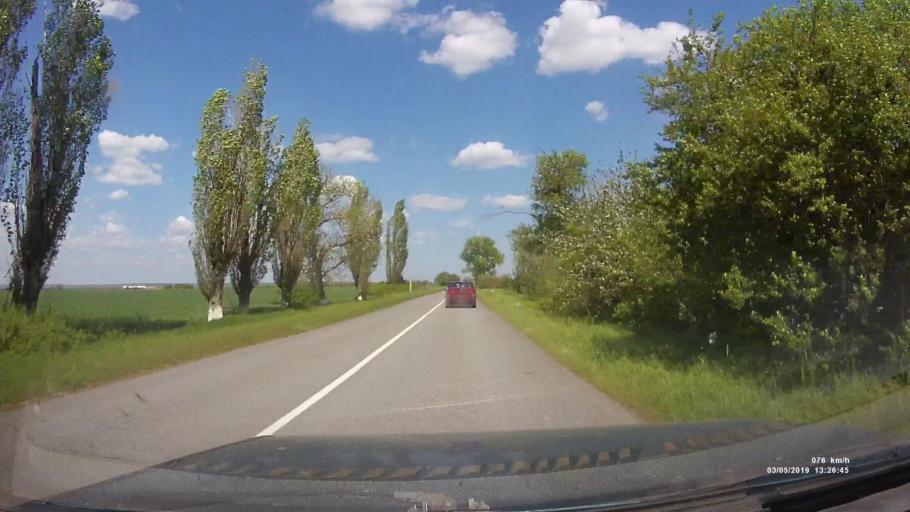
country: RU
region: Rostov
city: Semikarakorsk
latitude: 47.5733
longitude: 40.8251
